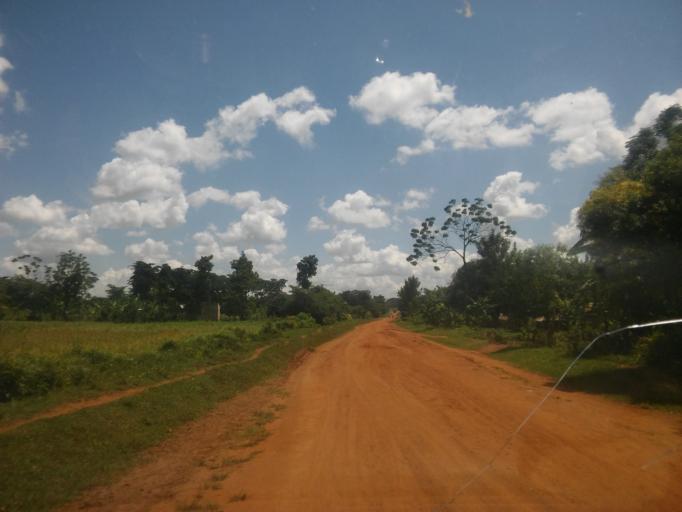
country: UG
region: Eastern Region
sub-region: Budaka District
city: Budaka
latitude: 1.1120
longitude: 33.9574
